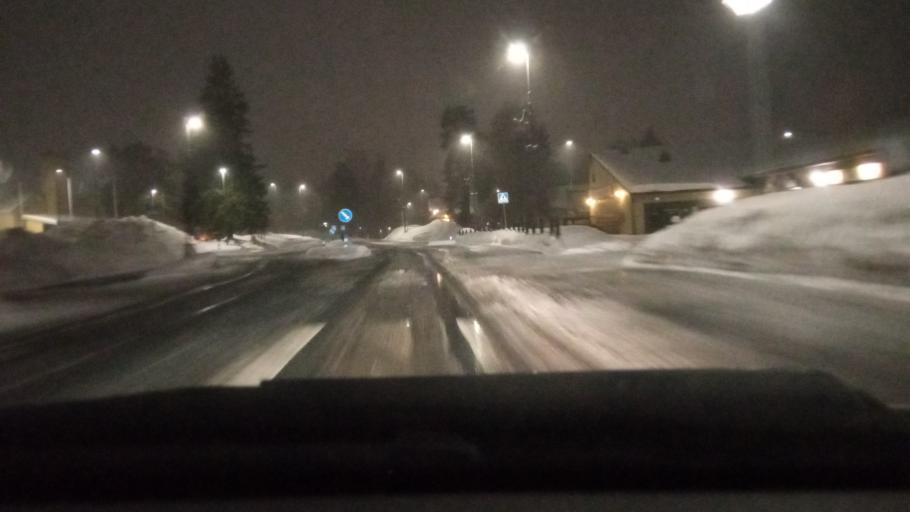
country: FI
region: Southern Ostrobothnia
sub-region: Jaerviseutu
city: Alajaervi
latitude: 63.0007
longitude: 23.8154
